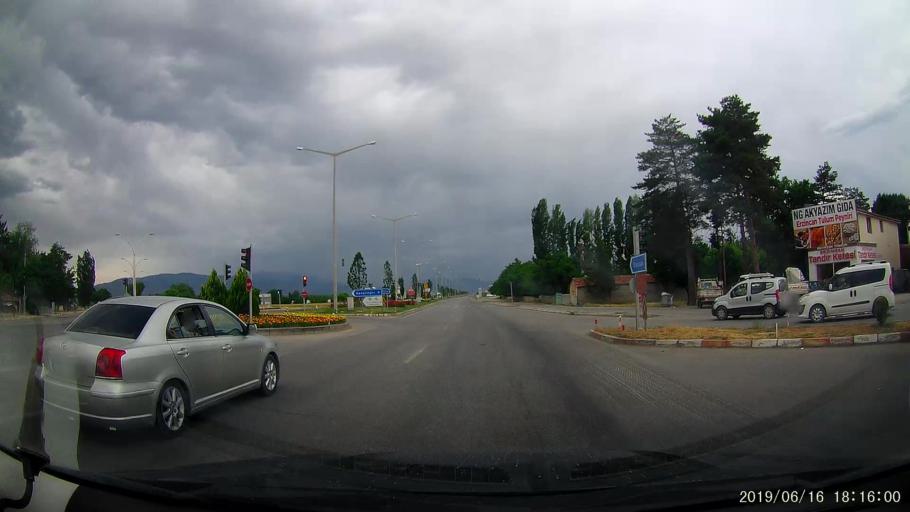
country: TR
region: Erzincan
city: Erzincan
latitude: 39.7266
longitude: 39.5527
